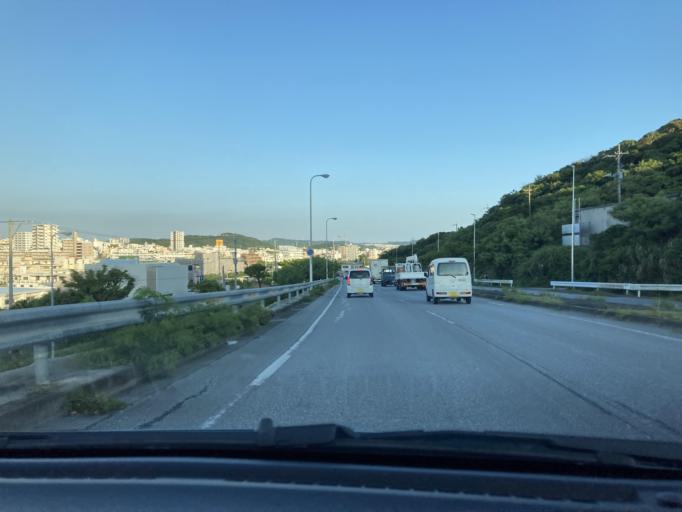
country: JP
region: Okinawa
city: Tomigusuku
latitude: 26.1927
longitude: 127.7005
